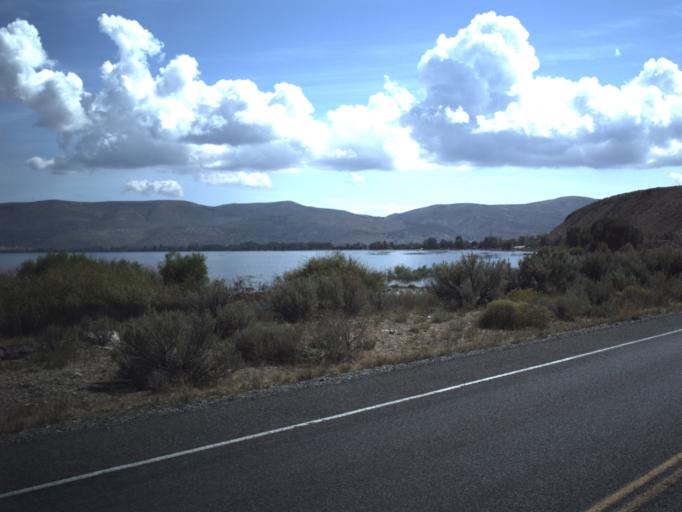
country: US
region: Utah
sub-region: Rich County
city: Randolph
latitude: 41.8543
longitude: -111.3634
